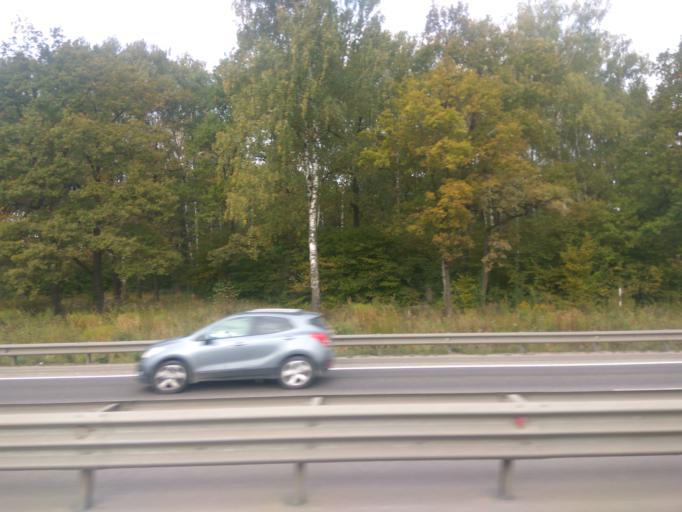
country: RU
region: Moskovskaya
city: Fryazino
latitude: 55.9459
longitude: 38.0426
